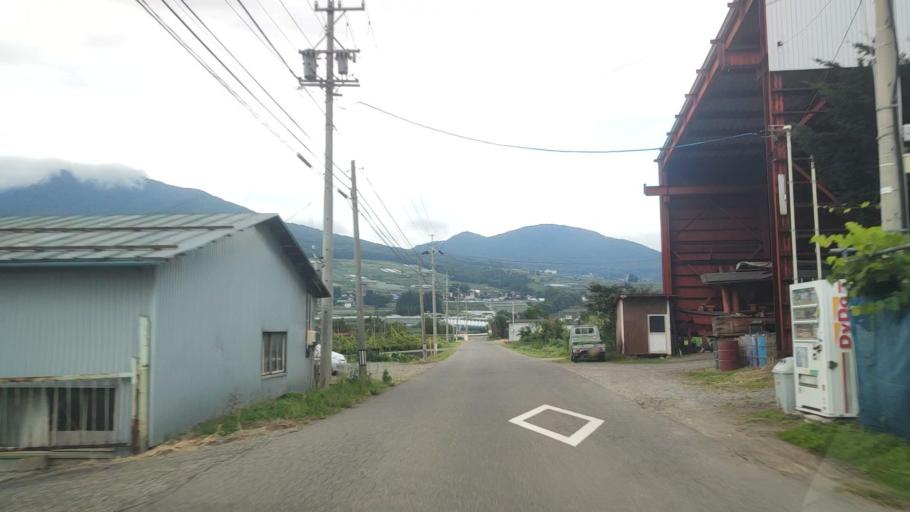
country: JP
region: Nagano
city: Nakano
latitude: 36.7629
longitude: 138.3931
